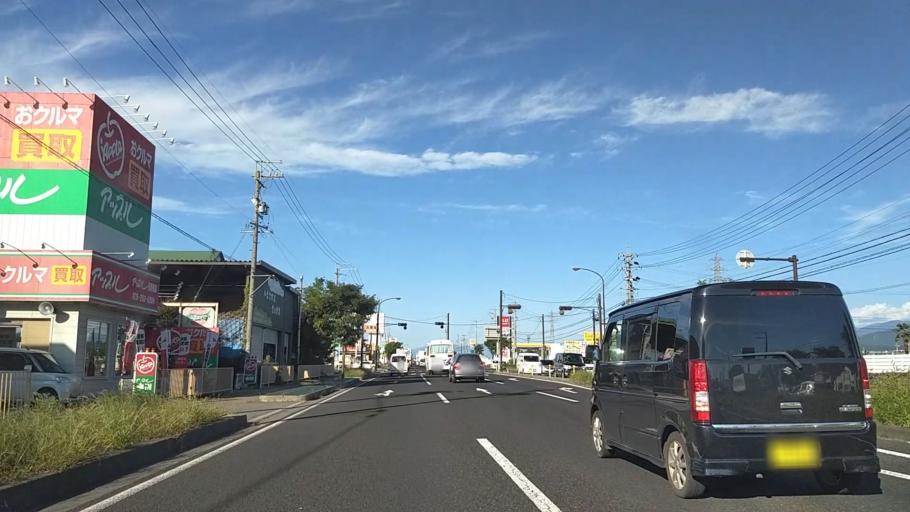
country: JP
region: Nagano
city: Nagano-shi
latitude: 36.5763
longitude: 138.1571
